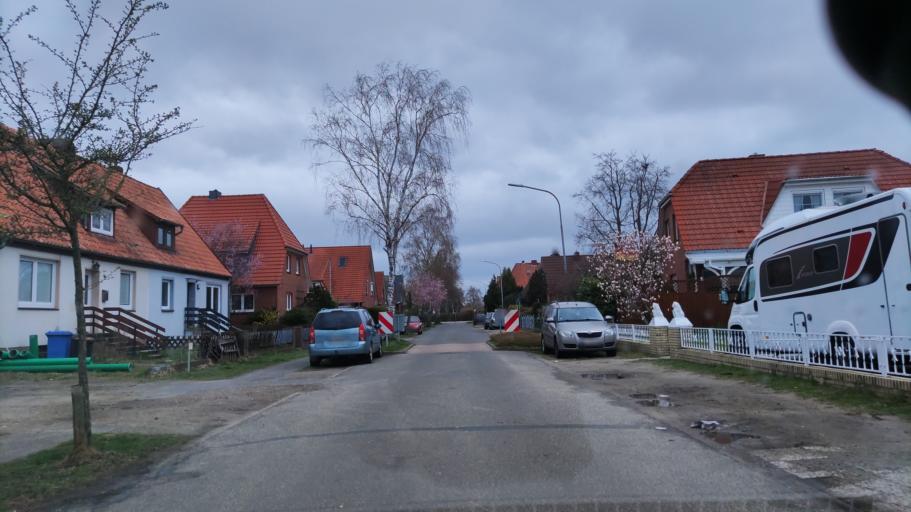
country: DE
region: Lower Saxony
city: Winsen
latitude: 53.3618
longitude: 10.2197
